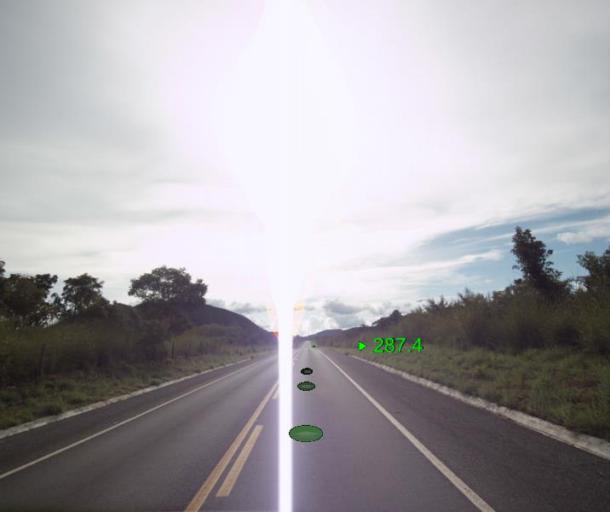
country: BR
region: Goias
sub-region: Barro Alto
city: Barro Alto
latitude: -15.1204
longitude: -48.7273
